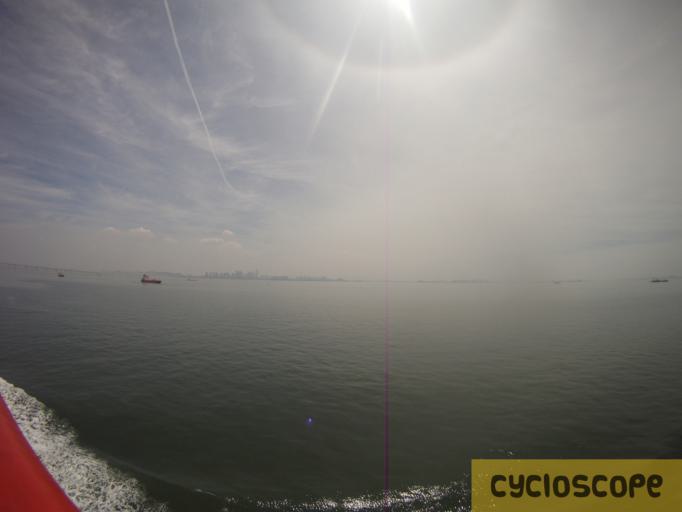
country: KR
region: Incheon
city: Incheon
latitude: 37.3973
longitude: 126.5567
